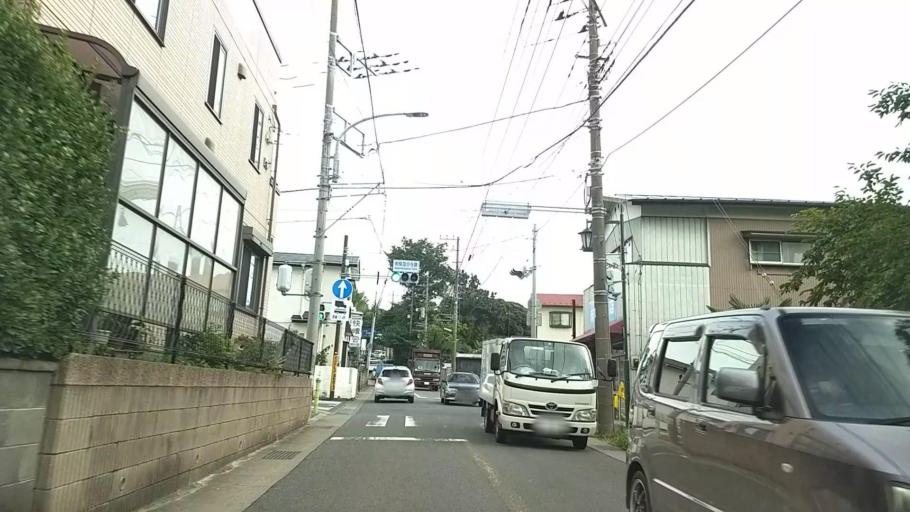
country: JP
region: Kanagawa
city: Zama
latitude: 35.4547
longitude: 139.3991
